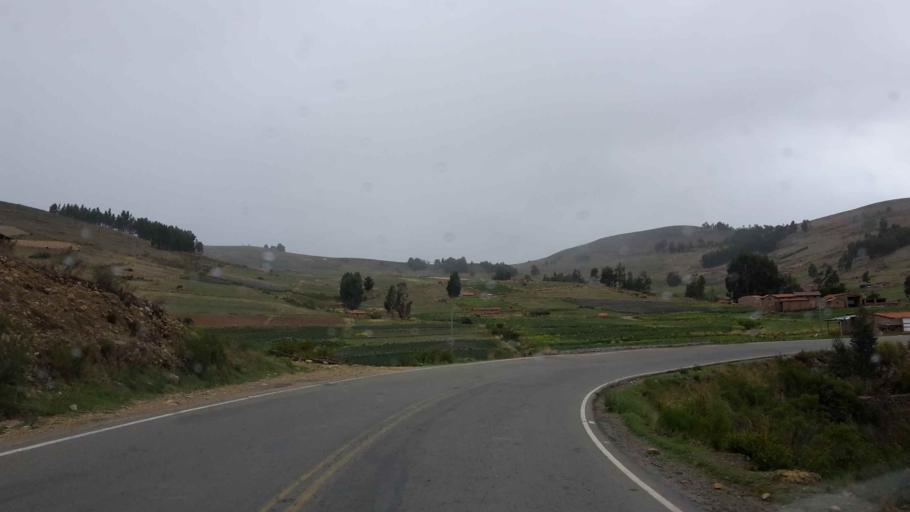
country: BO
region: Cochabamba
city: Arani
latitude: -17.4607
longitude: -65.6777
